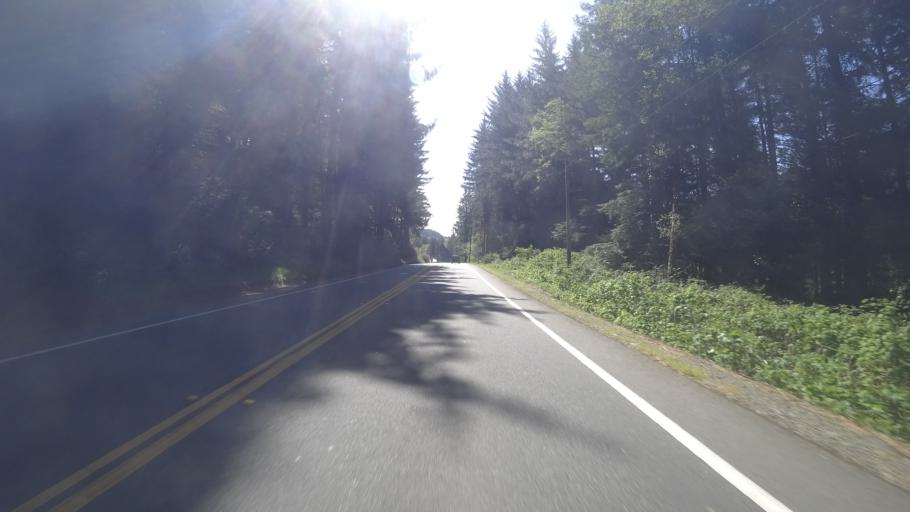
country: US
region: California
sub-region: Del Norte County
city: Bertsch-Oceanview
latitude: 41.5801
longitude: -124.0778
